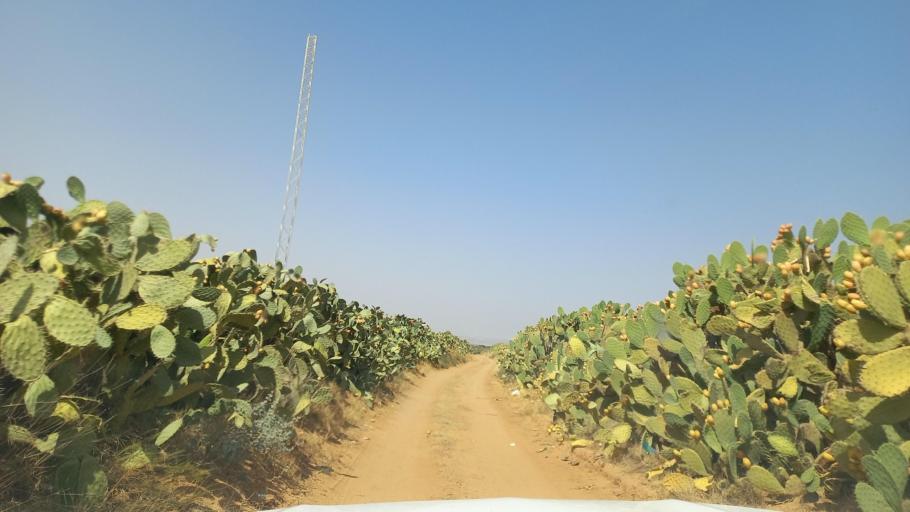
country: TN
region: Al Qasrayn
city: Kasserine
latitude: 35.2417
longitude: 9.0567
